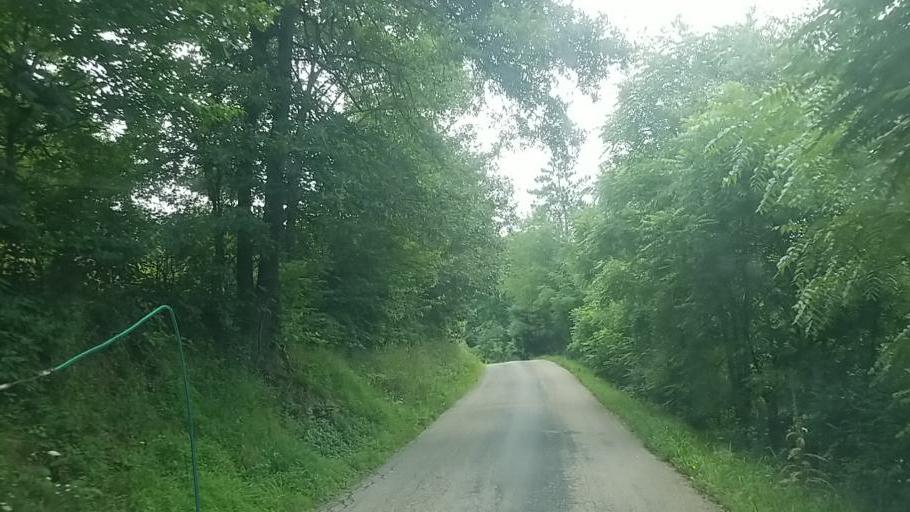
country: US
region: Ohio
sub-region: Muskingum County
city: Frazeysburg
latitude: 40.2371
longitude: -82.2133
